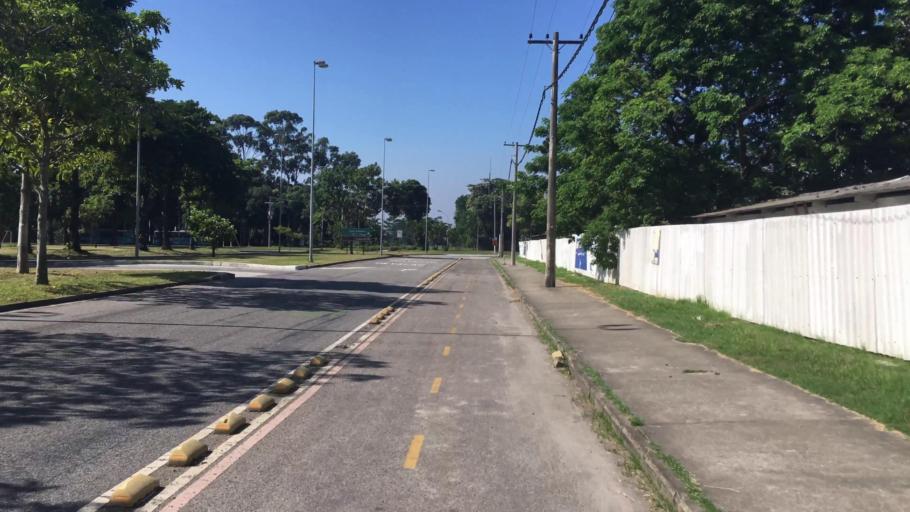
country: BR
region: Rio de Janeiro
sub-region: Rio De Janeiro
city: Rio de Janeiro
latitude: -22.8406
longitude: -43.2295
